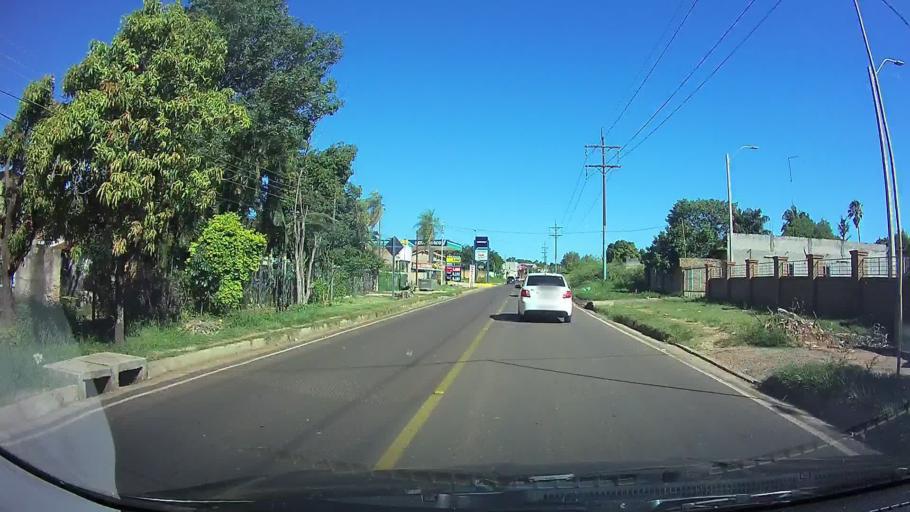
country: PY
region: Central
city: Fernando de la Mora
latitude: -25.3029
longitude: -57.5332
